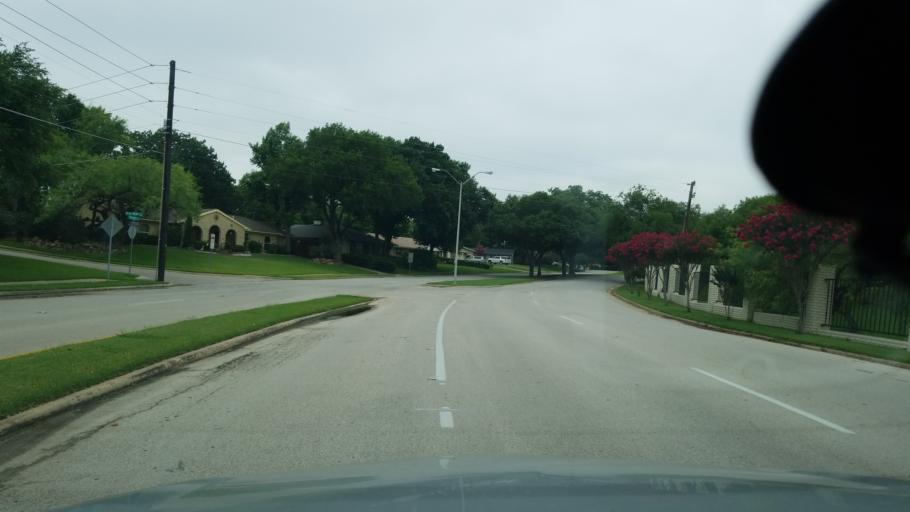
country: US
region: Texas
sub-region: Dallas County
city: Irving
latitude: 32.8521
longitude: -96.9454
